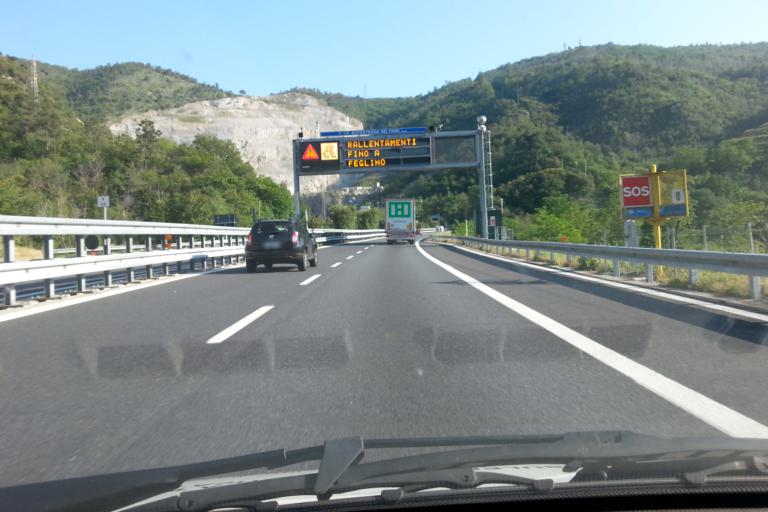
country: IT
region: Liguria
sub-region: Provincia di Savona
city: Valle di Vado
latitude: 44.2537
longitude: 8.4068
